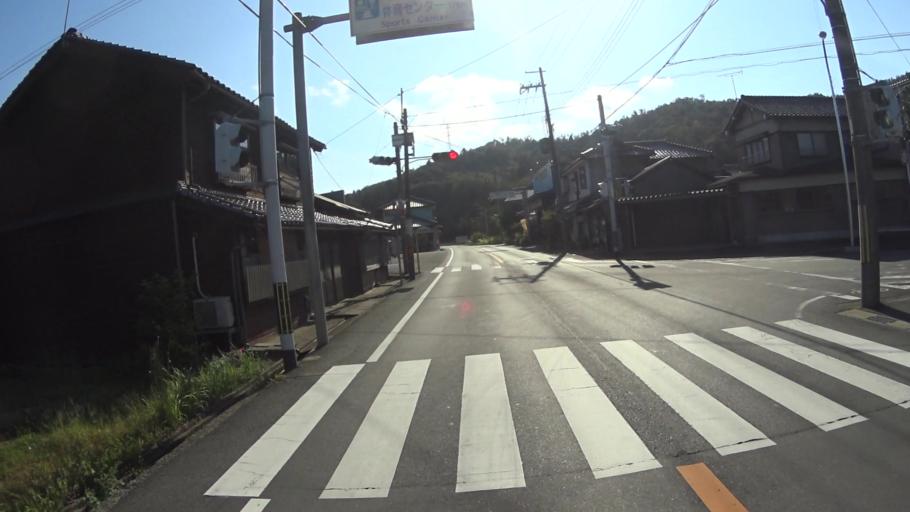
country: JP
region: Kyoto
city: Miyazu
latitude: 35.6679
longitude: 135.0253
